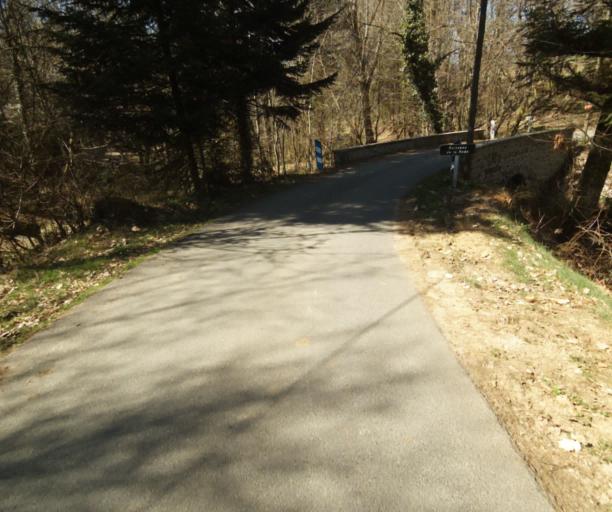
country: FR
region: Limousin
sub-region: Departement de la Correze
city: Saint-Clement
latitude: 45.3131
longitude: 1.7118
